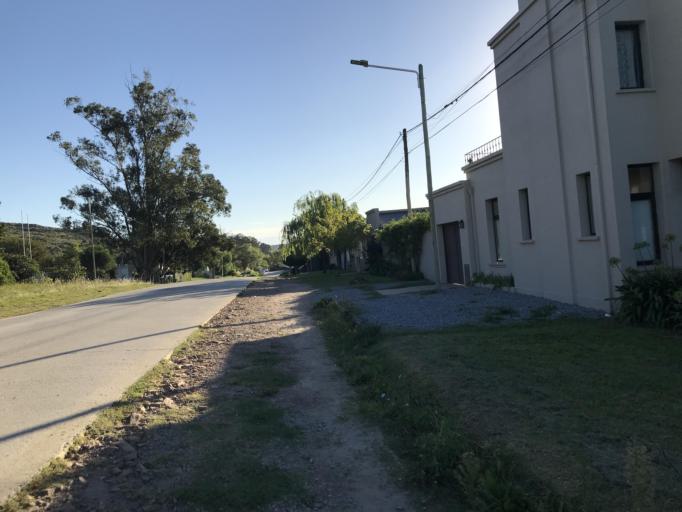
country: AR
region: Buenos Aires
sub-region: Partido de Tandil
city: Tandil
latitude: -37.3386
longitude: -59.1150
